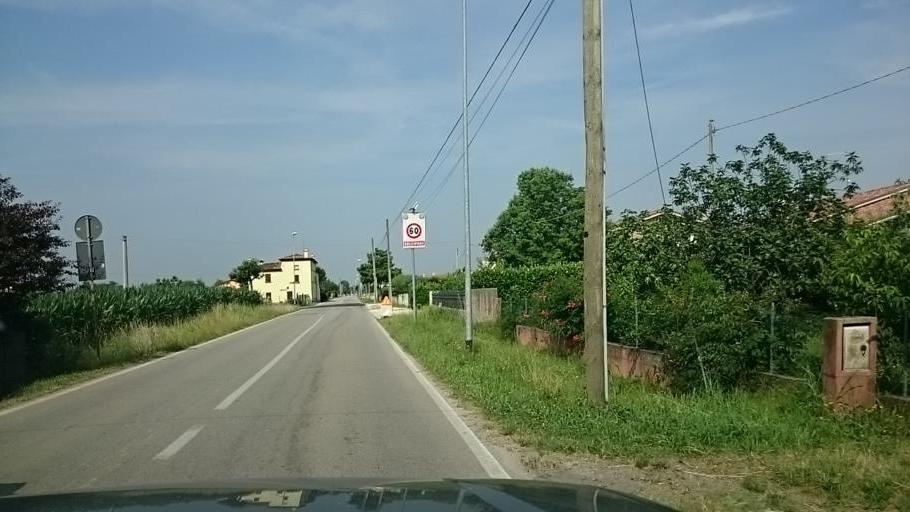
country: IT
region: Veneto
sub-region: Provincia di Treviso
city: Castello di Godego
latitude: 45.6879
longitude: 11.8710
